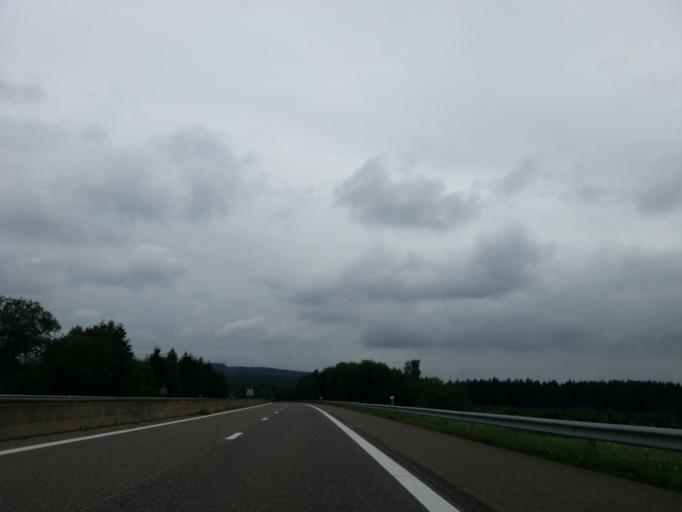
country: BE
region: Wallonia
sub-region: Province de Liege
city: Saint-Vith
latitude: 50.3260
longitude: 6.0898
